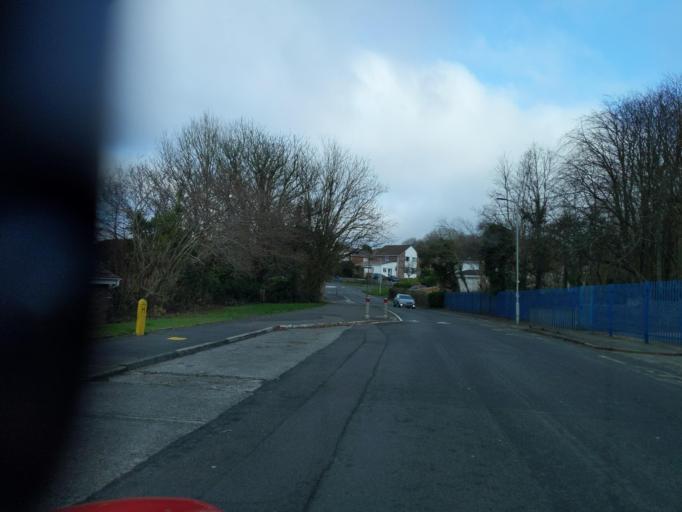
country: GB
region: England
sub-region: Plymouth
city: Plymouth
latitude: 50.4325
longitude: -4.1162
